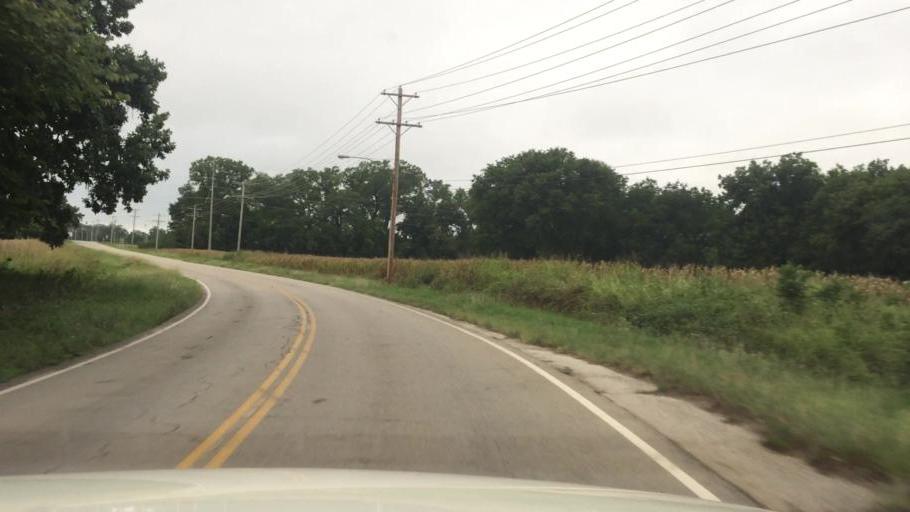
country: US
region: Kansas
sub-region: Montgomery County
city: Coffeyville
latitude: 37.0352
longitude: -95.5842
